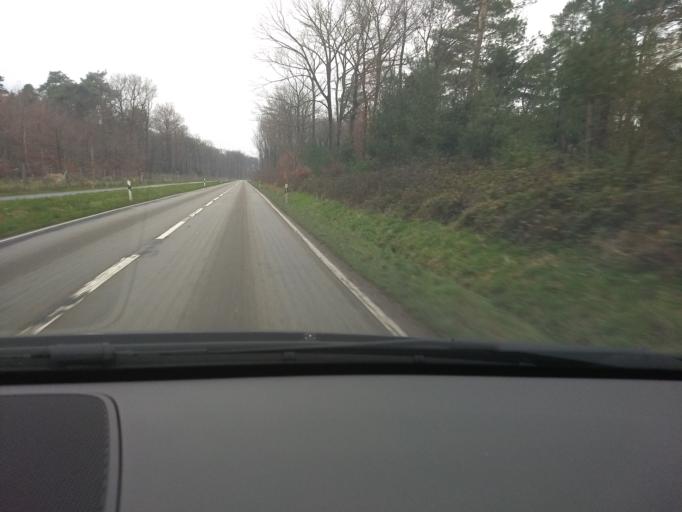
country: DE
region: North Rhine-Westphalia
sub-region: Regierungsbezirk Munster
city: Borken
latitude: 51.8662
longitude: 6.8890
